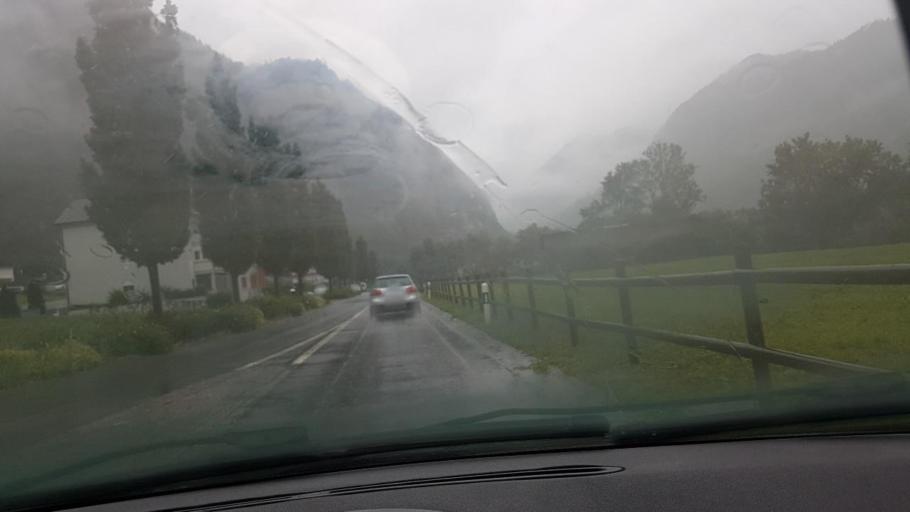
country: LI
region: Balzers
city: Balzers
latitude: 47.0628
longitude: 9.5102
